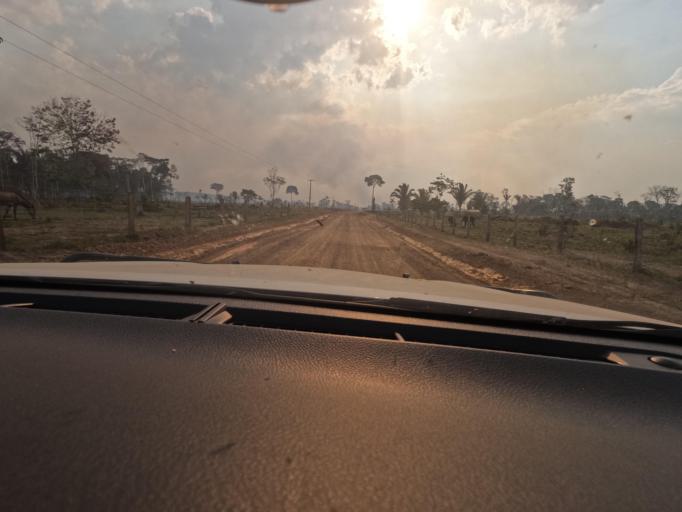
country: BR
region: Rondonia
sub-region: Porto Velho
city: Porto Velho
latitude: -8.6383
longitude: -63.1772
